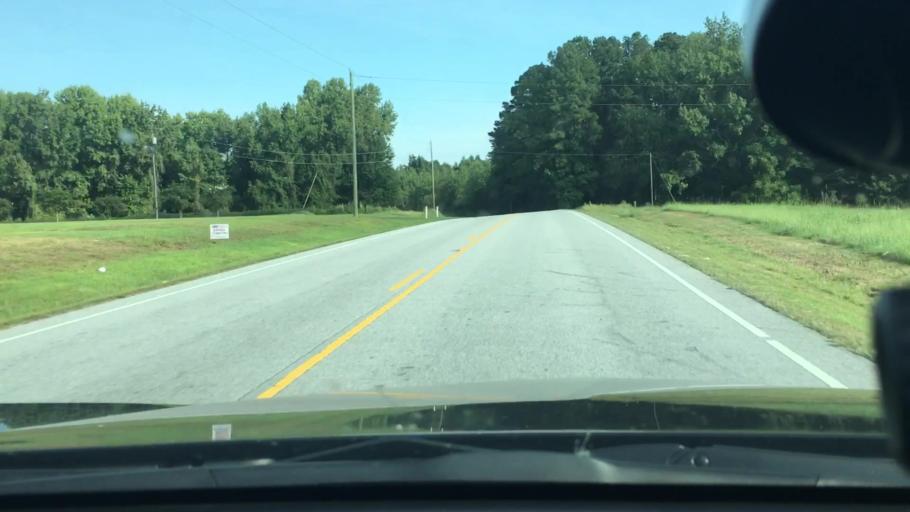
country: US
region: North Carolina
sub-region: Edgecombe County
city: Pinetops
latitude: 35.7325
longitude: -77.5328
